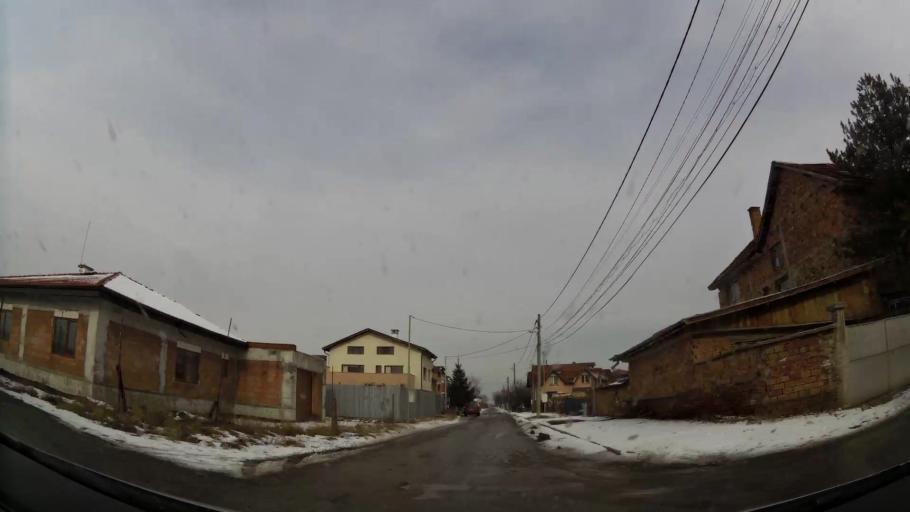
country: BG
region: Sofia-Capital
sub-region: Stolichna Obshtina
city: Sofia
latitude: 42.7128
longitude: 23.4003
